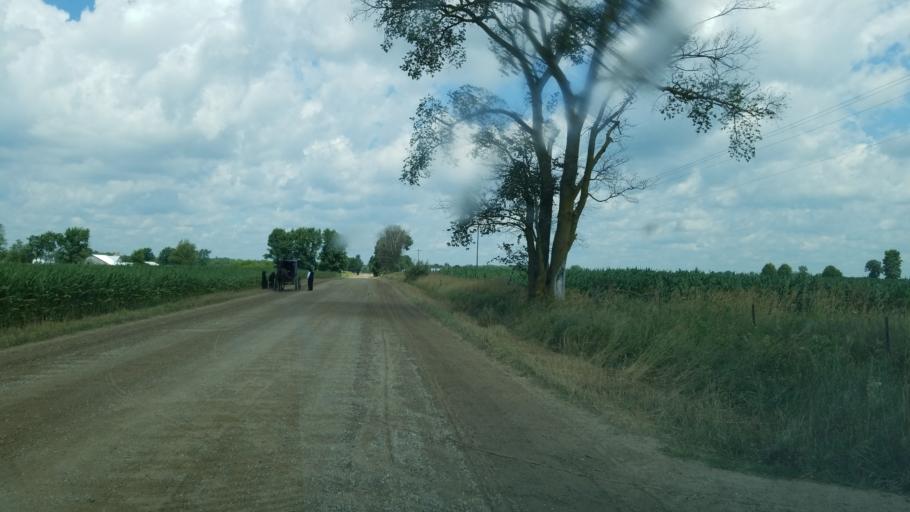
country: US
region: Michigan
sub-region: Mecosta County
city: Canadian Lakes
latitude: 43.5457
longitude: -85.3924
